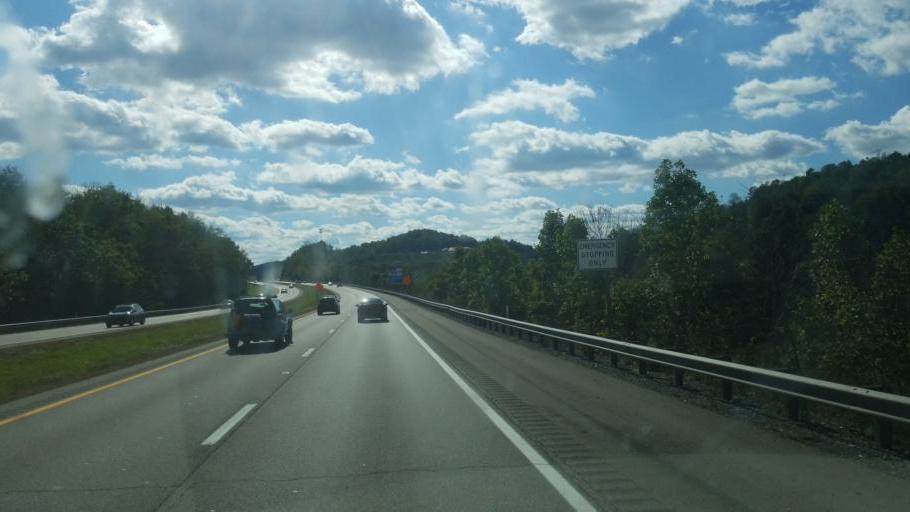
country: US
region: West Virginia
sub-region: Monongalia County
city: Brookhaven
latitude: 39.6261
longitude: -79.9056
